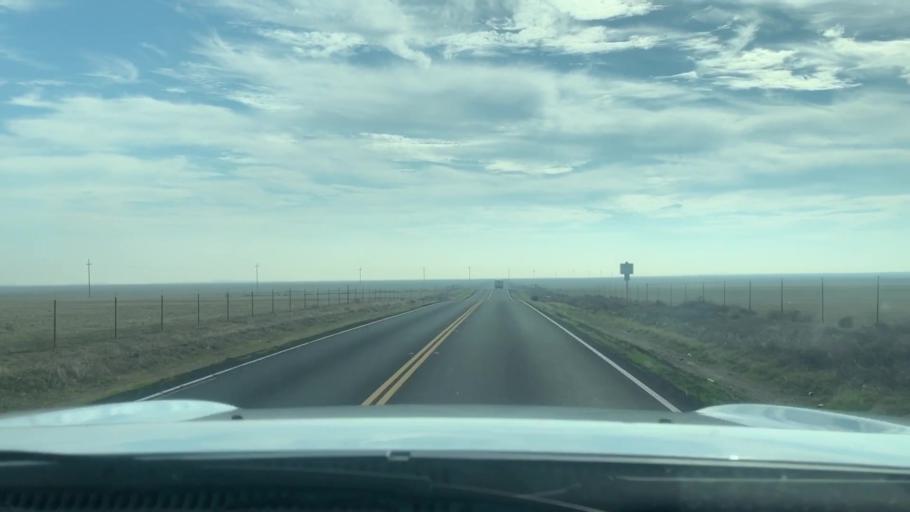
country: US
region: California
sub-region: Kern County
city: Lost Hills
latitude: 35.5949
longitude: -119.8432
